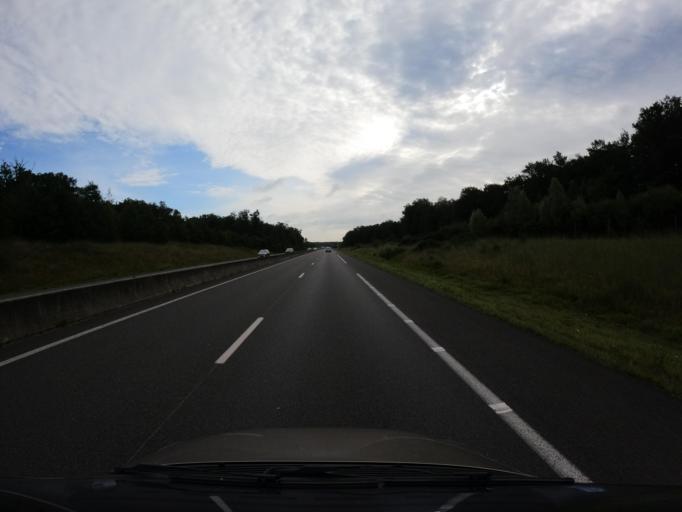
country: FR
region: Centre
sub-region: Departement d'Indre-et-Loire
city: Langeais
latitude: 47.3172
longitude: 0.3225
